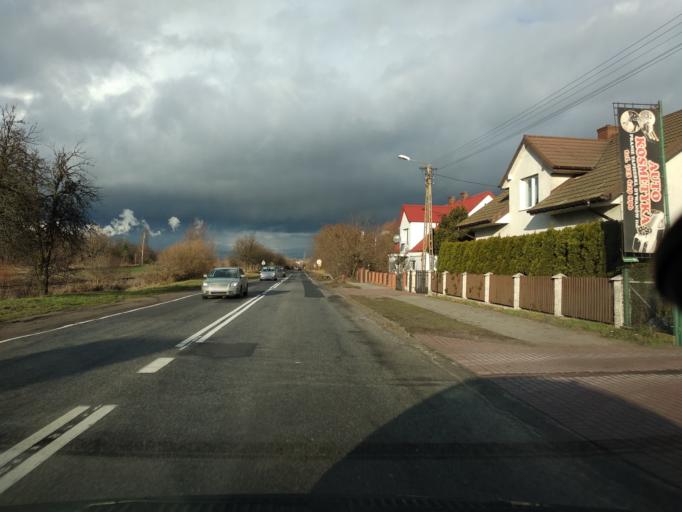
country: PL
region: Greater Poland Voivodeship
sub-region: Konin
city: Konin
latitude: 52.2690
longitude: 18.2670
